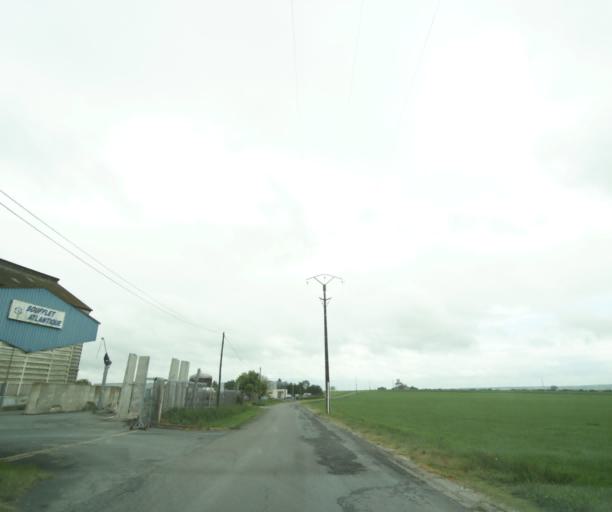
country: FR
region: Poitou-Charentes
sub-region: Departement de la Charente-Maritime
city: Perignac
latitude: 45.6531
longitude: -0.5056
